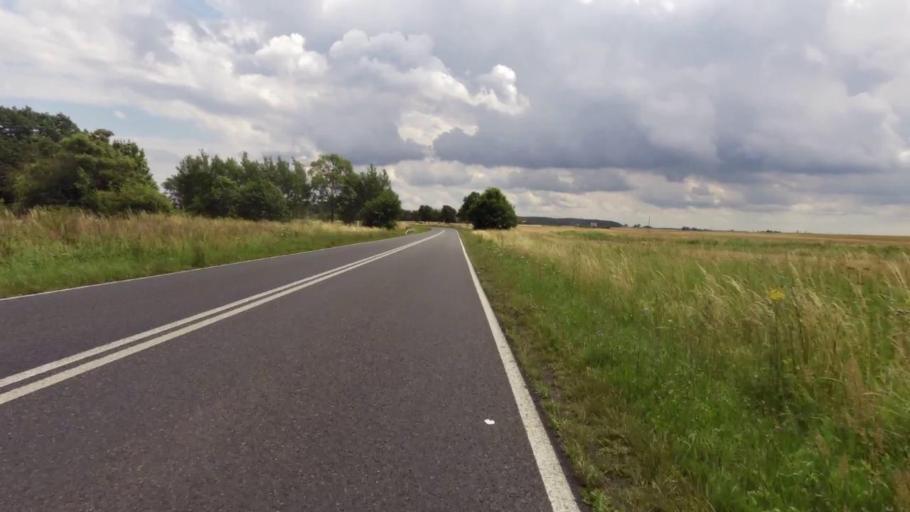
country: PL
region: West Pomeranian Voivodeship
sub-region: Powiat pyrzycki
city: Lipiany
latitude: 52.9975
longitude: 15.0423
